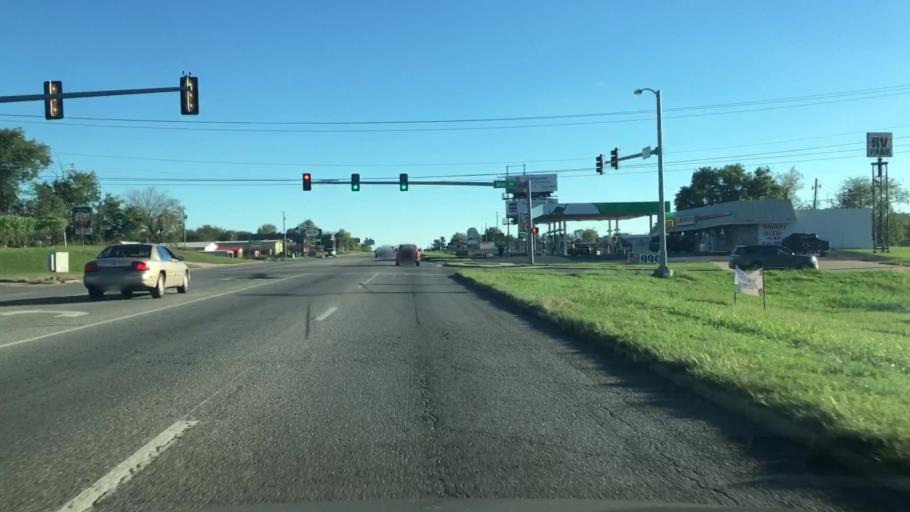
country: US
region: Oklahoma
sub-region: Cherokee County
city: Park Hill
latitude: 35.8713
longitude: -94.9763
